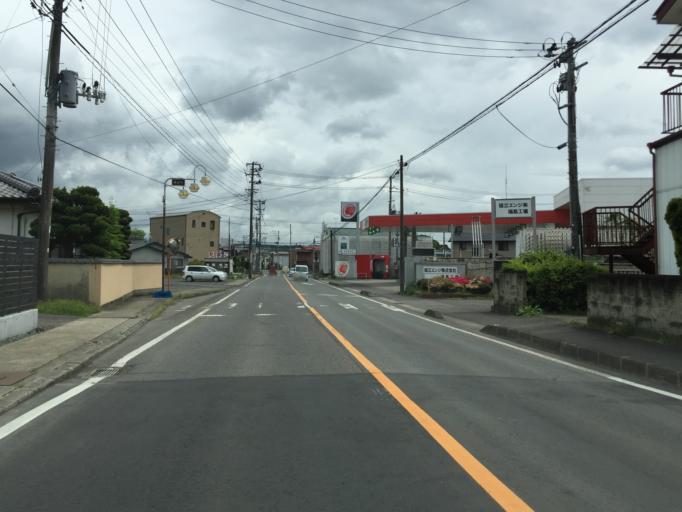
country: JP
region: Fukushima
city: Ishikawa
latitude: 37.0378
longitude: 140.3795
